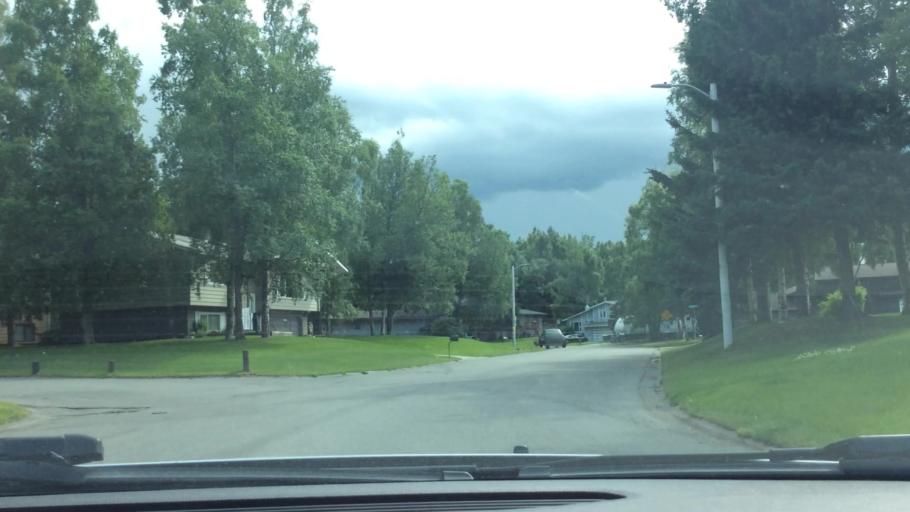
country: US
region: Alaska
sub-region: Anchorage Municipality
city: Elmendorf Air Force Base
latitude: 61.2216
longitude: -149.7527
